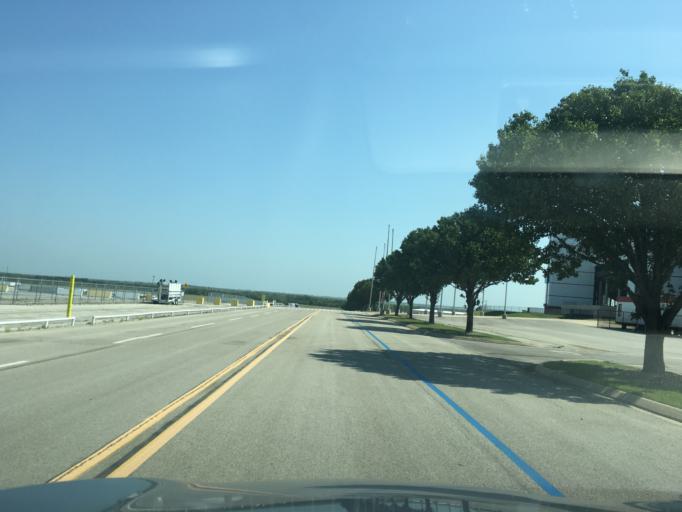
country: US
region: Texas
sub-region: Denton County
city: Justin
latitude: 33.0394
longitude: -97.2852
